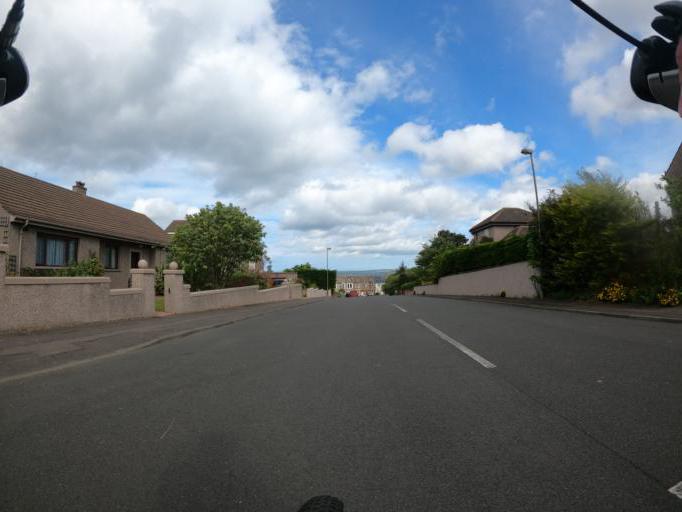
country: GB
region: Scotland
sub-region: East Lothian
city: Musselburgh
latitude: 55.9475
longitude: -3.0842
